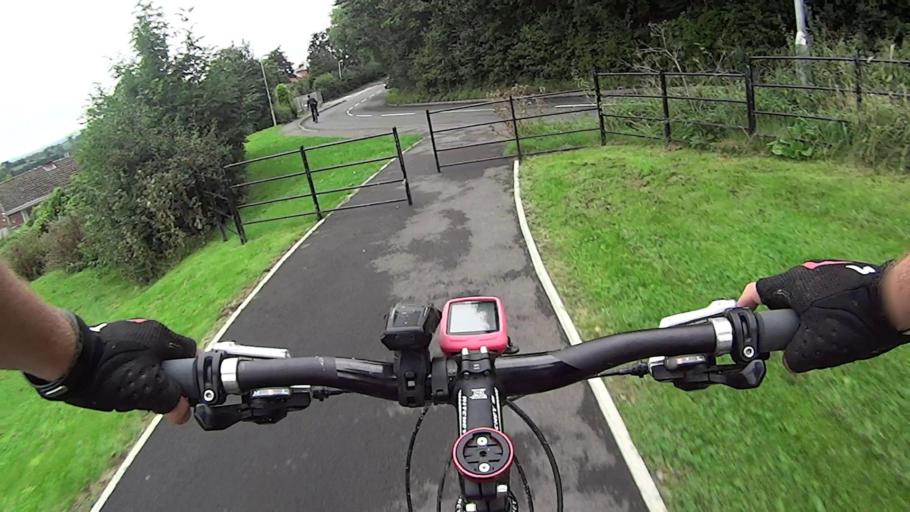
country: GB
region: England
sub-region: Worcestershire
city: Tenbury Wells
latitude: 52.3067
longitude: -2.5987
